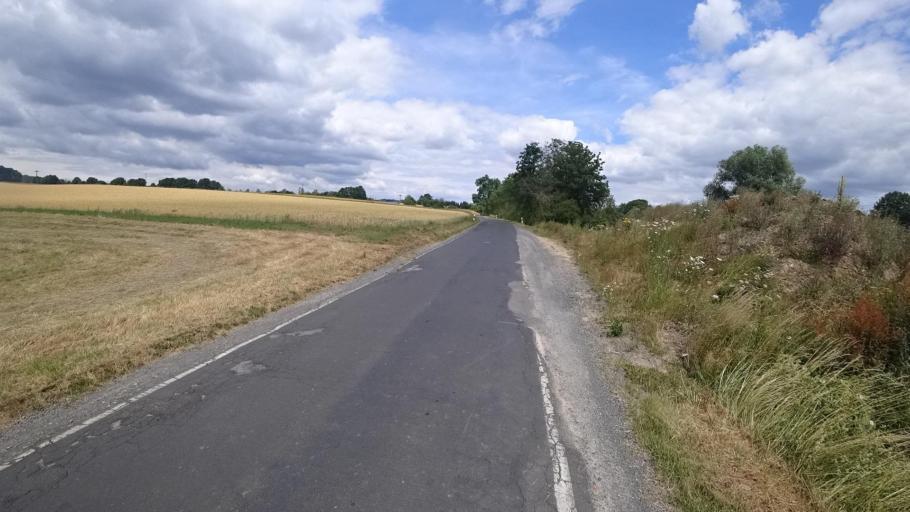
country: DE
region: Rheinland-Pfalz
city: Forstmehren
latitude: 50.7054
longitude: 7.5317
